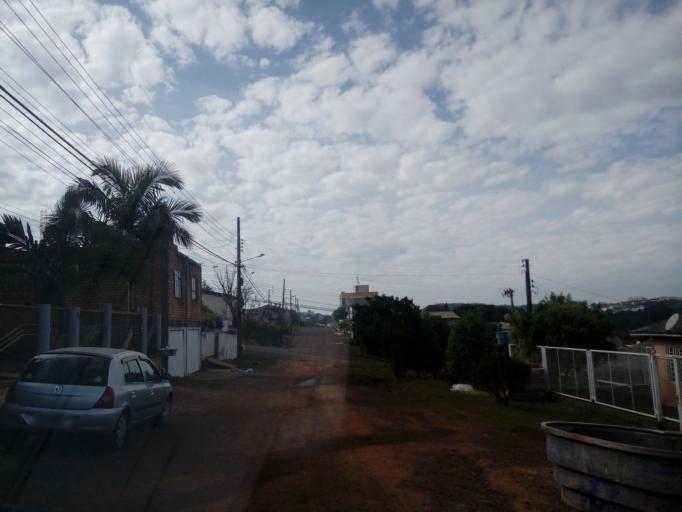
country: BR
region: Santa Catarina
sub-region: Chapeco
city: Chapeco
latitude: -27.1227
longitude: -52.6231
